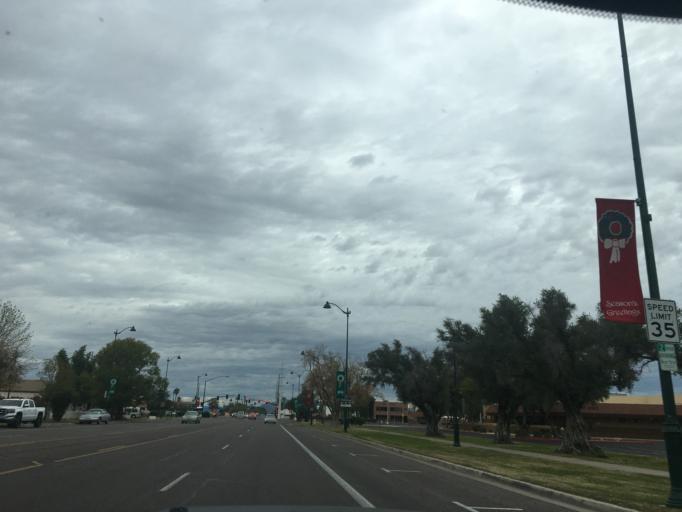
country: US
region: Arizona
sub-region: Maricopa County
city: Mesa
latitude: 33.4204
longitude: -111.8314
